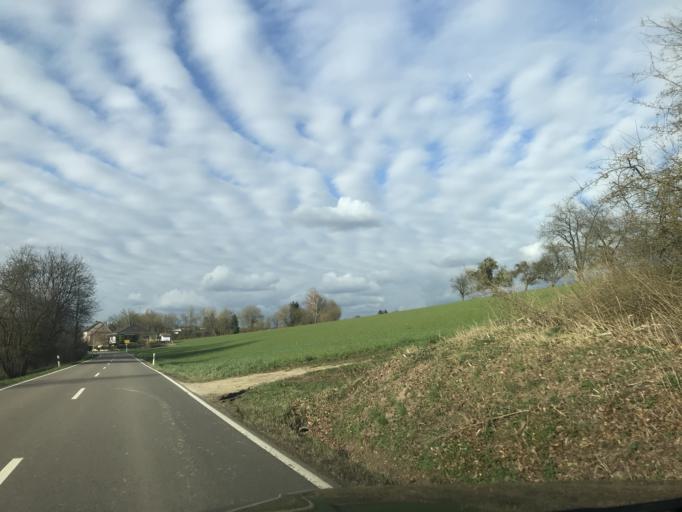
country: DE
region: Saarland
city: Blieskastel
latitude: 49.1896
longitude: 7.2499
